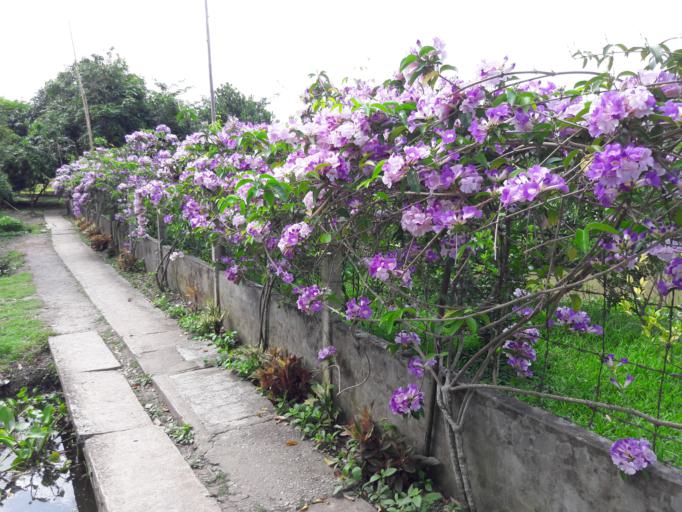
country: VN
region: Can Tho
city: Cai Rang
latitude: 10.0286
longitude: 105.7329
